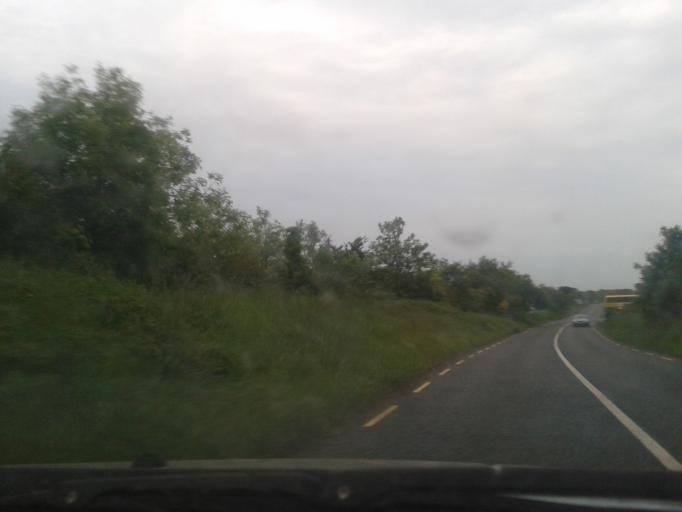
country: IE
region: Leinster
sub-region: Dublin City
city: Finglas
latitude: 53.4207
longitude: -6.3068
